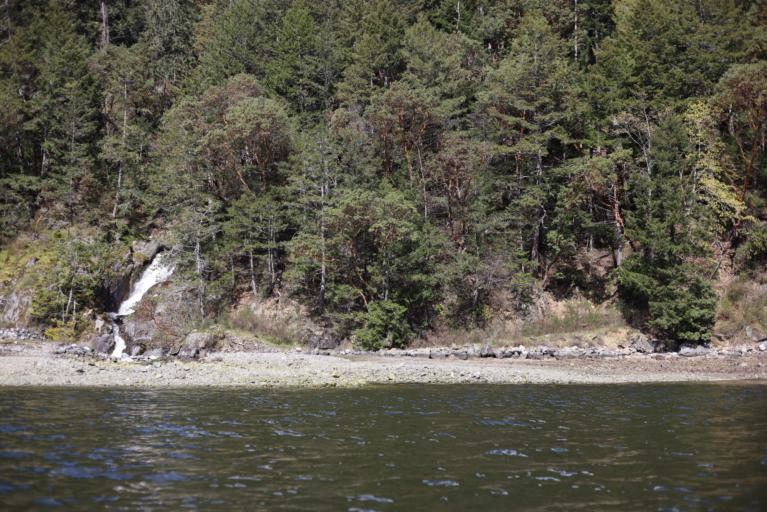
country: CA
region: British Columbia
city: Langford
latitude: 48.5593
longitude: -123.5353
